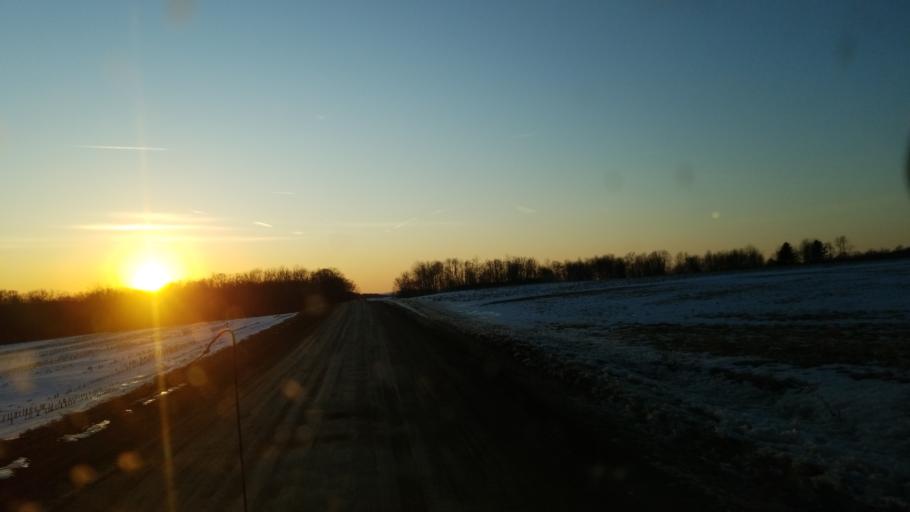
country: US
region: Pennsylvania
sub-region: Tioga County
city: Westfield
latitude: 42.0128
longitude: -77.6634
